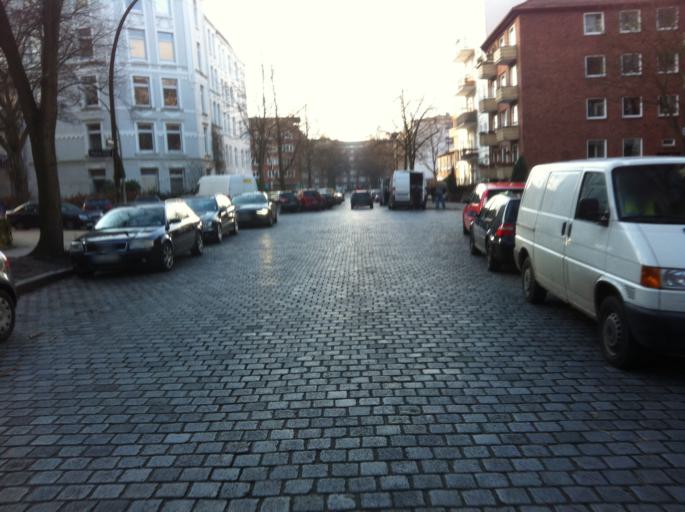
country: DE
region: Hamburg
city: St. Pauli
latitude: 53.5665
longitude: 9.9480
